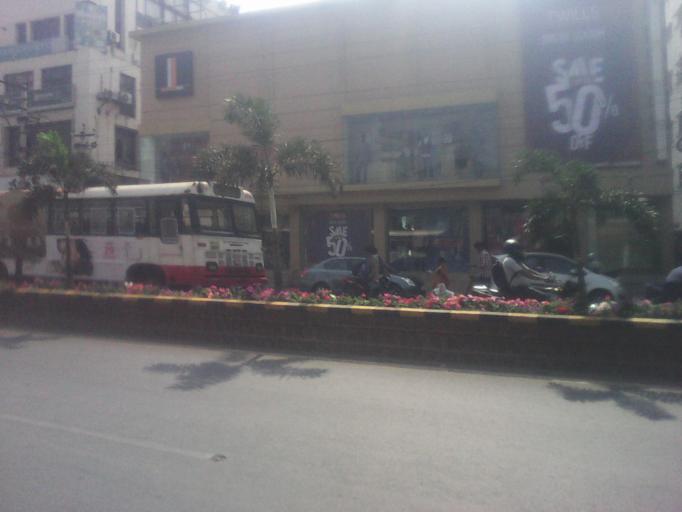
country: IN
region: Andhra Pradesh
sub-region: Krishna
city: Yanamalakuduru
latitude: 16.4997
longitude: 80.6488
